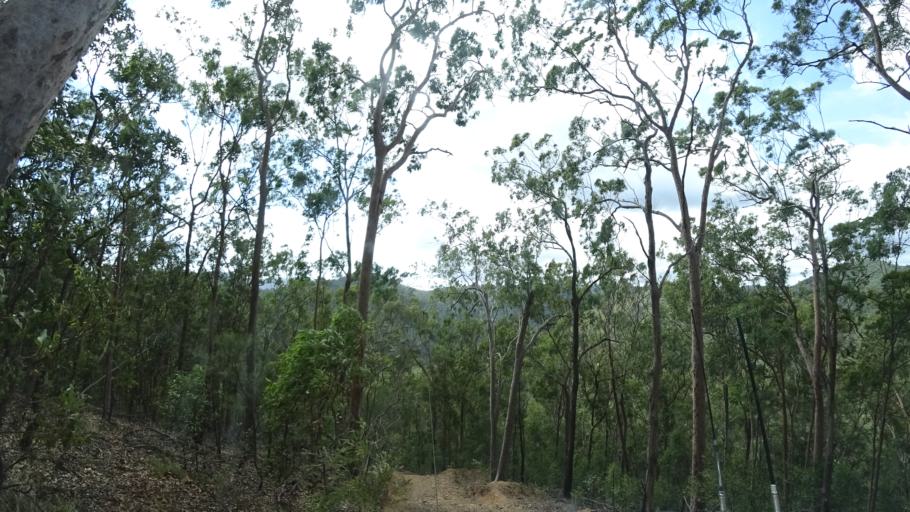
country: AU
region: Queensland
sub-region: Moreton Bay
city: Highvale
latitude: -27.3750
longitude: 152.7374
